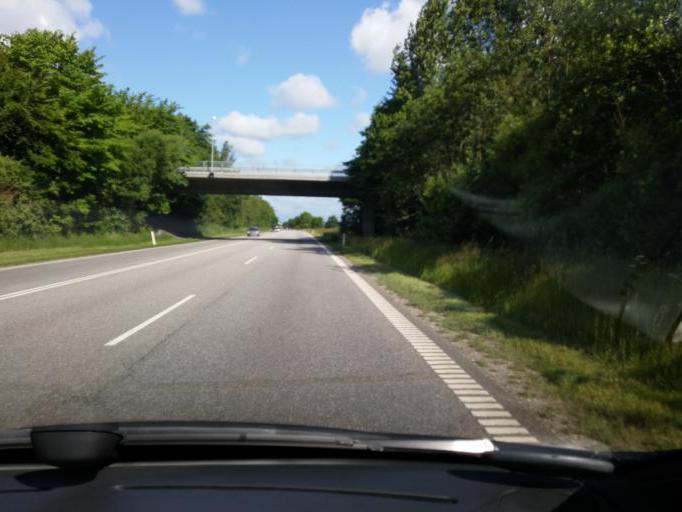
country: DK
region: Capital Region
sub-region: Hillerod Kommune
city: Hillerod
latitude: 55.8891
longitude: 12.2936
